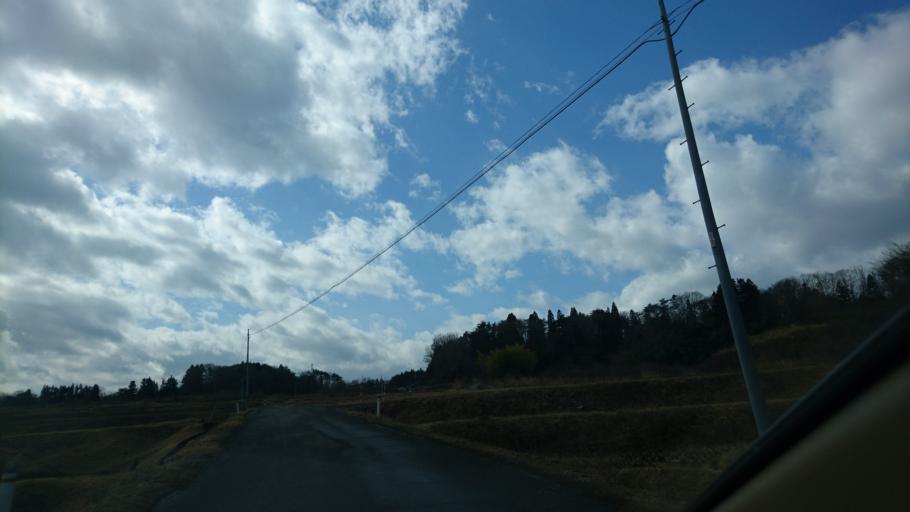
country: JP
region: Iwate
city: Ichinoseki
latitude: 38.9554
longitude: 141.1138
